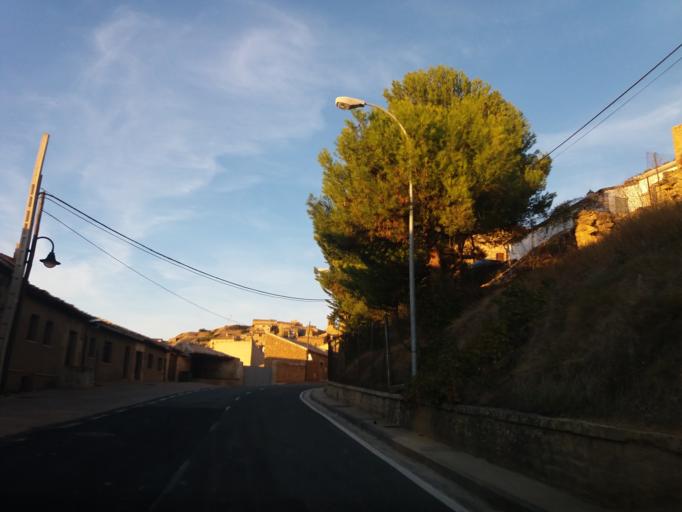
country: ES
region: Navarre
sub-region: Provincia de Navarra
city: San Martin de Unx
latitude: 42.5225
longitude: -1.5640
